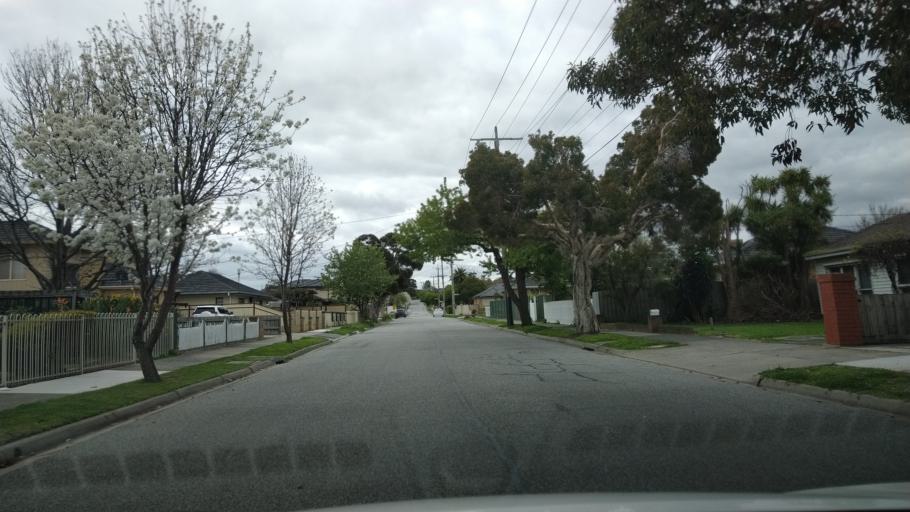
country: AU
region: Victoria
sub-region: Greater Dandenong
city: Noble Park
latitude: -37.9719
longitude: 145.1602
